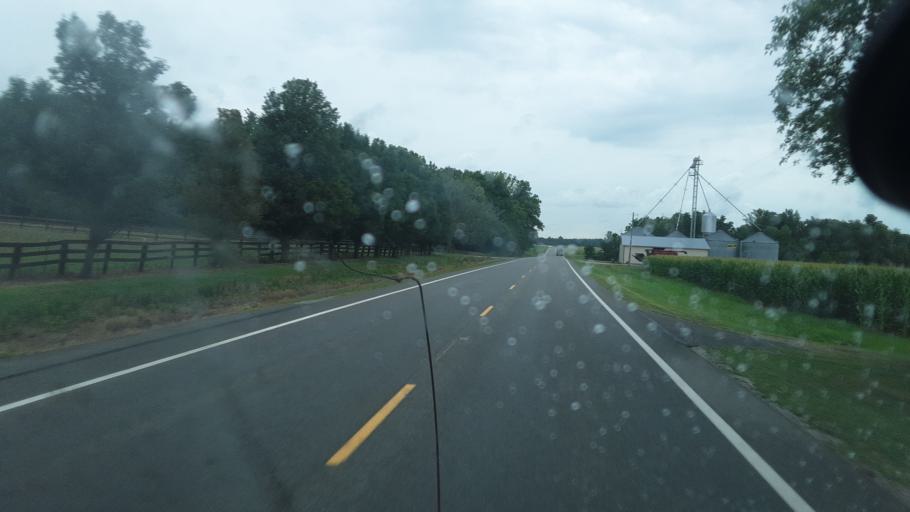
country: US
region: Ohio
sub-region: Williams County
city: Bryan
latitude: 41.4140
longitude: -84.6222
